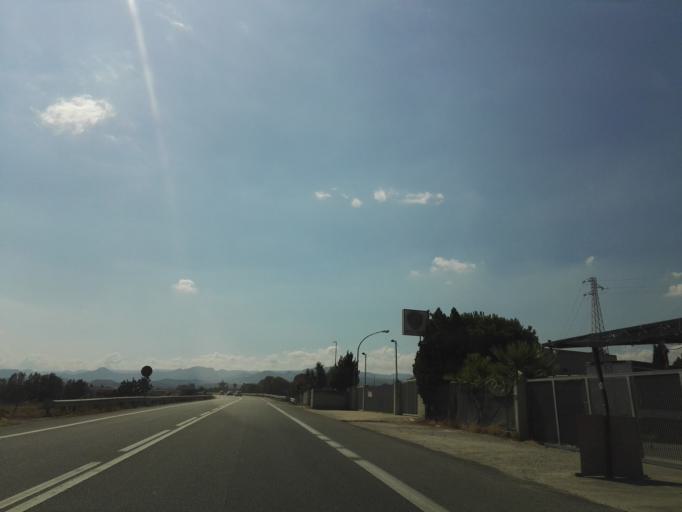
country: IT
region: Calabria
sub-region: Provincia di Reggio Calabria
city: Marina di Gioiosa Ionica
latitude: 38.3068
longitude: 16.3462
